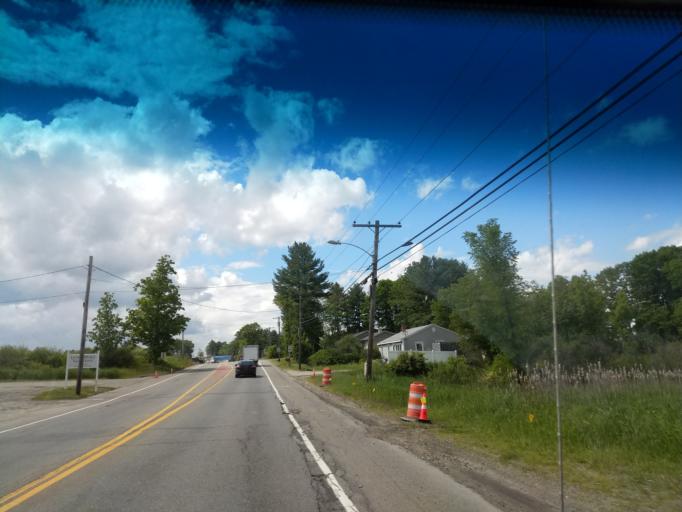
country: US
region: Maine
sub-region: Cumberland County
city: Westbrook
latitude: 43.6835
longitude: -70.3816
